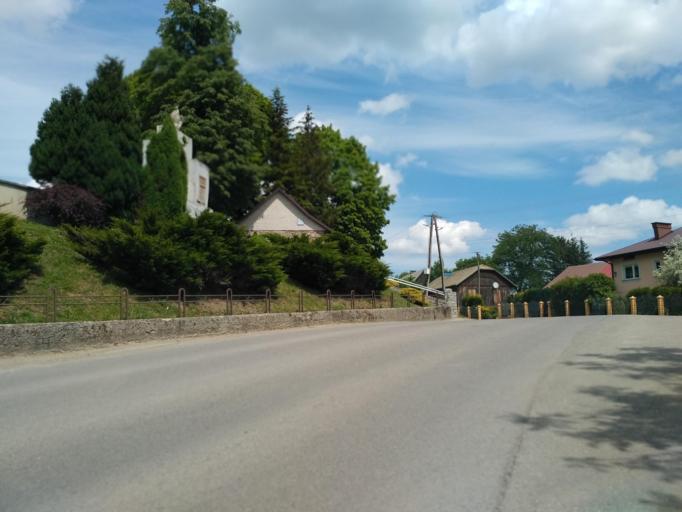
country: PL
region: Subcarpathian Voivodeship
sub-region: Powiat krosnienski
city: Chorkowka
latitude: 49.6106
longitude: 21.6449
